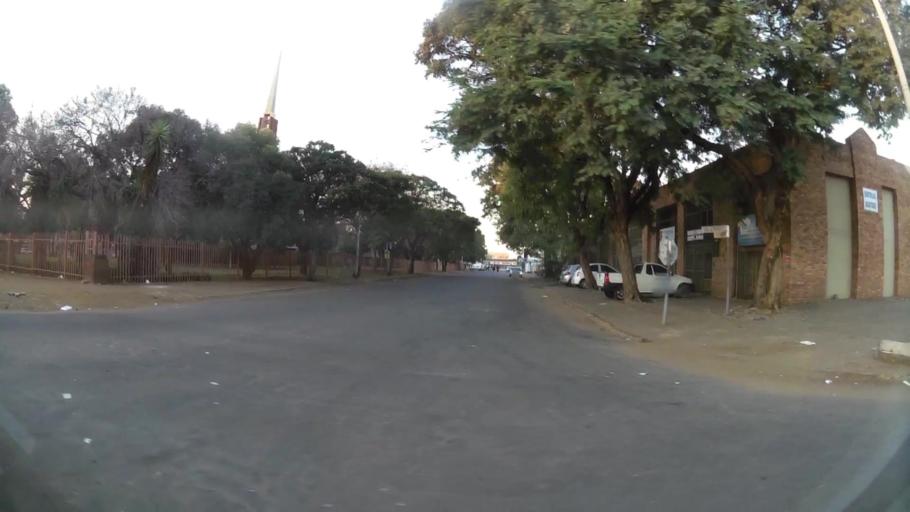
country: ZA
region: North-West
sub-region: Bojanala Platinum District Municipality
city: Rustenburg
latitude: -25.6720
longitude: 27.2398
